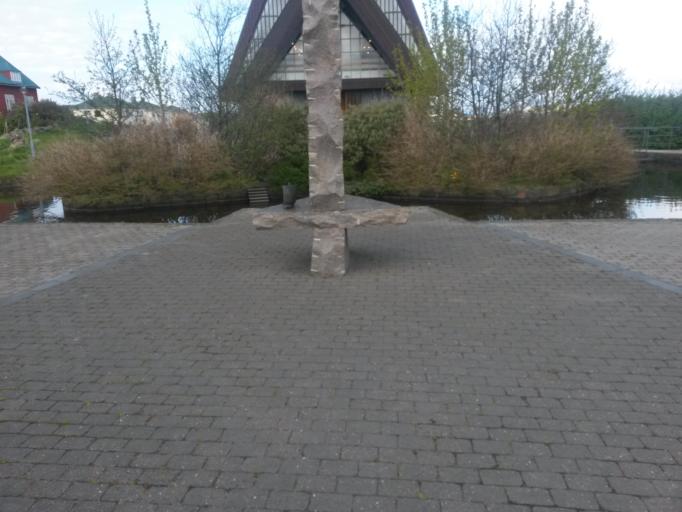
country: FO
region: Streymoy
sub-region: Torshavn
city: Torshavn
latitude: 62.0072
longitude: -6.7852
